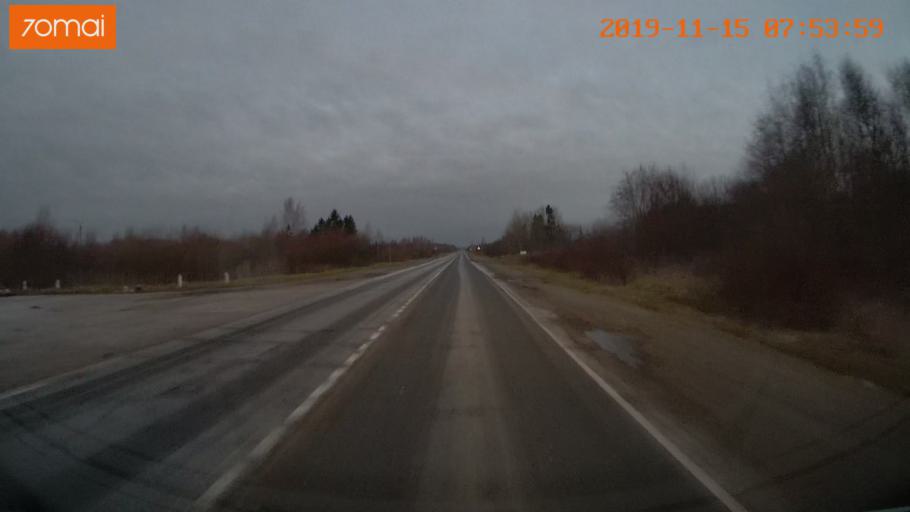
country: RU
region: Vologda
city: Cherepovets
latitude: 58.8943
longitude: 38.1810
